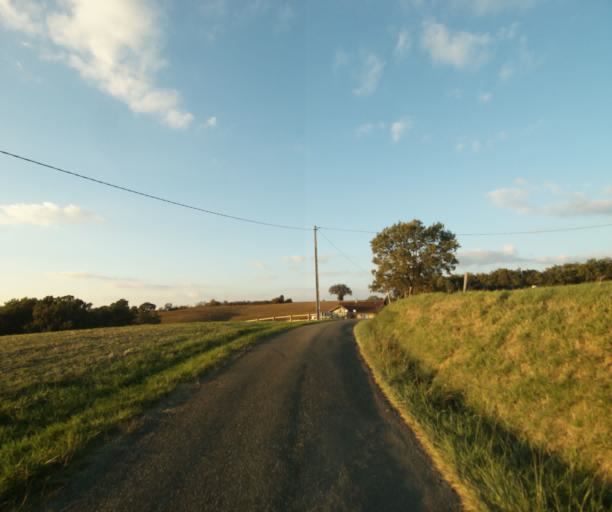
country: FR
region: Midi-Pyrenees
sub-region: Departement du Gers
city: Vic-Fezensac
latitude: 43.7520
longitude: 0.1967
